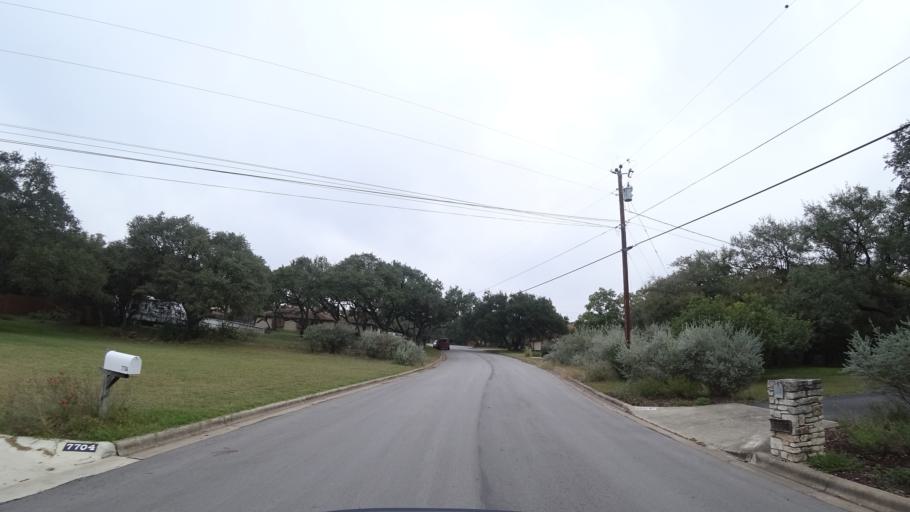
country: US
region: Texas
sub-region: Travis County
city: Shady Hollow
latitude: 30.2196
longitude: -97.9110
